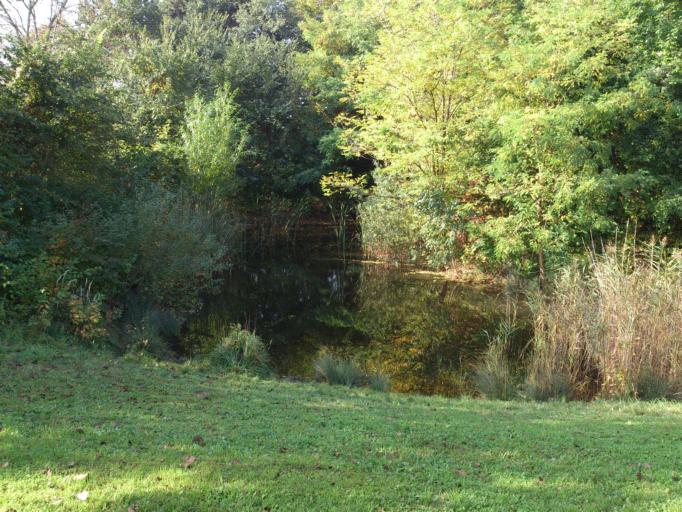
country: AT
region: Lower Austria
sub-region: Politischer Bezirk Mistelbach
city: Wolkersdorf im Weinviertel
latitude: 48.3786
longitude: 16.5239
